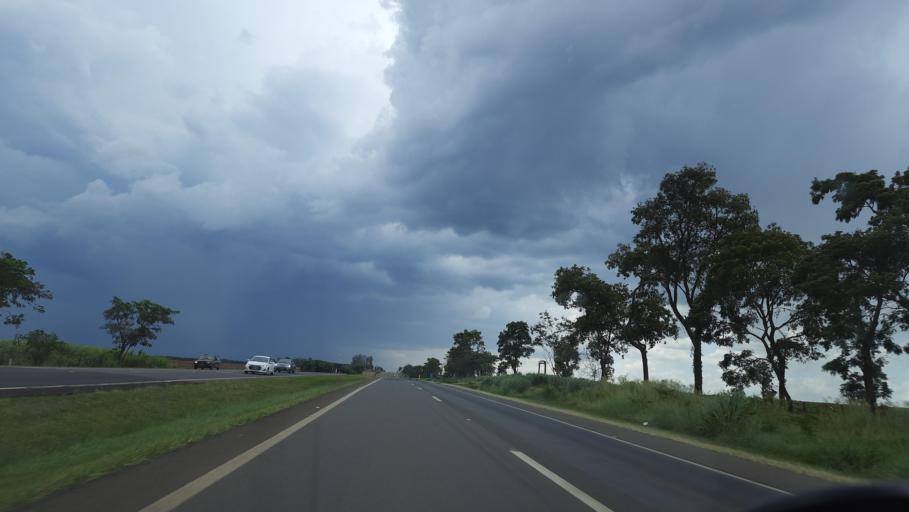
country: BR
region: Sao Paulo
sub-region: Aguai
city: Aguai
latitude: -22.0230
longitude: -47.0342
